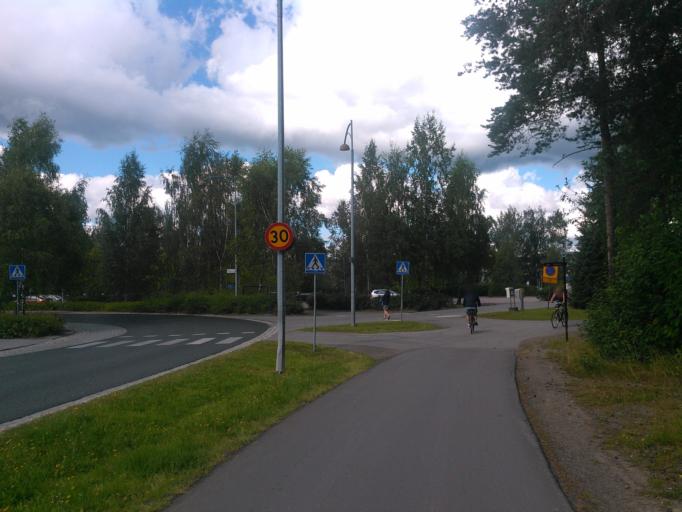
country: SE
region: Vaesterbotten
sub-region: Umea Kommun
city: Umea
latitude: 63.8190
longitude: 20.3039
